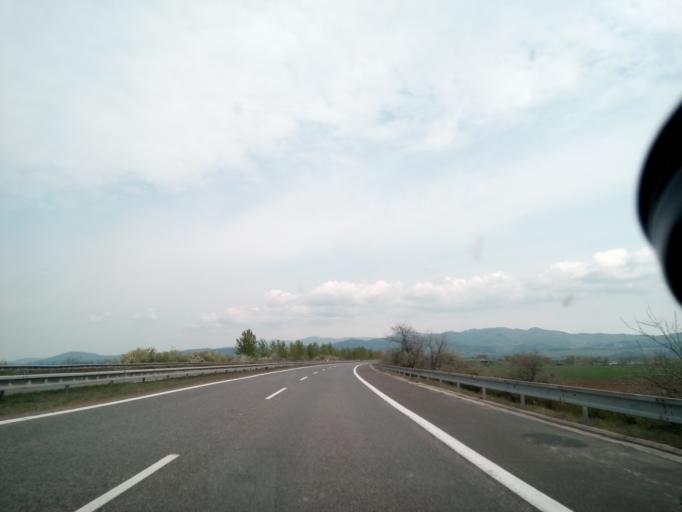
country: SK
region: Trnavsky
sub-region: Okres Trnava
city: Piestany
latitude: 48.6460
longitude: 17.8242
